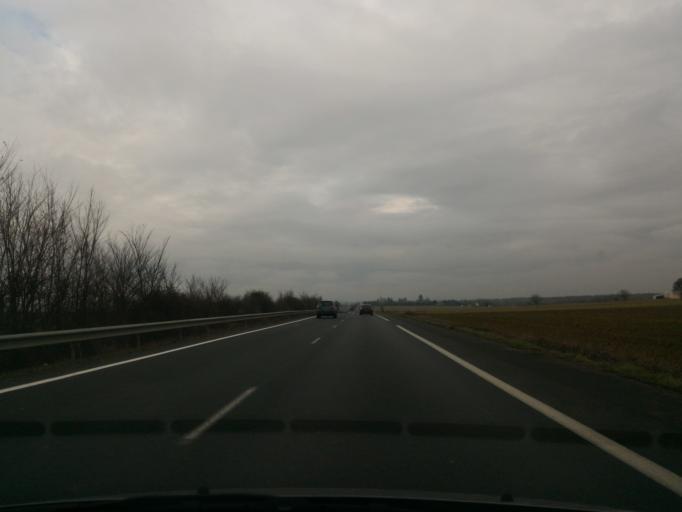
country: FR
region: Poitou-Charentes
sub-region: Departement de la Vienne
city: Celle-Levescault
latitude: 46.3934
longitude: 0.2269
